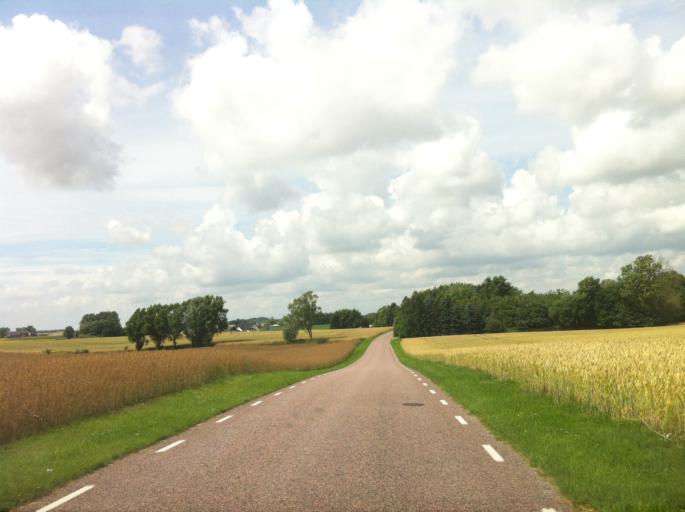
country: SE
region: Skane
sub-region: Skurups Kommun
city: Skurup
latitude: 55.4214
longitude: 13.4480
